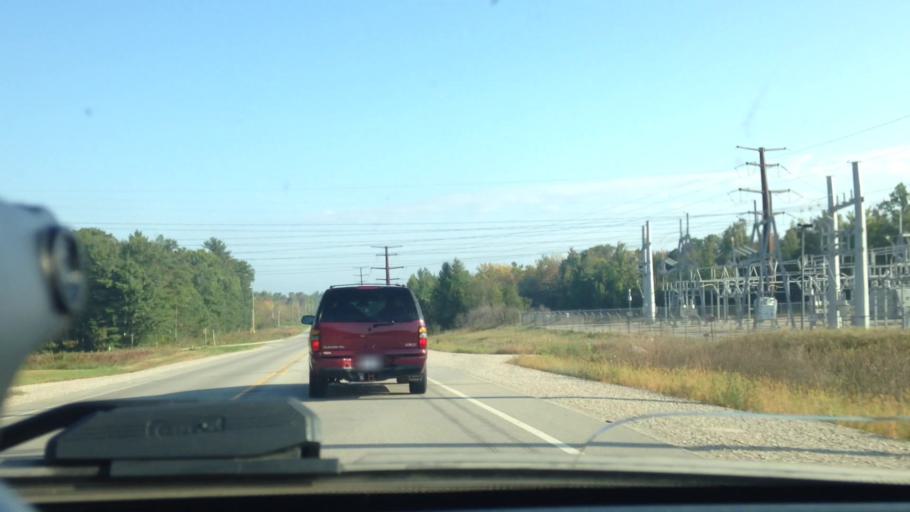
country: US
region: Wisconsin
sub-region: Marinette County
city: Peshtigo
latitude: 45.1759
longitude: -87.9959
